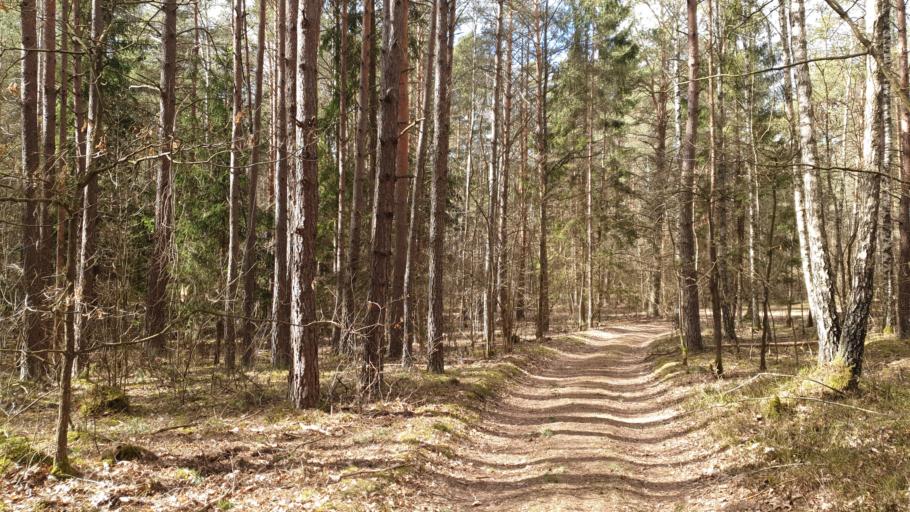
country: LT
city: Grigiskes
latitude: 54.7270
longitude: 25.0331
